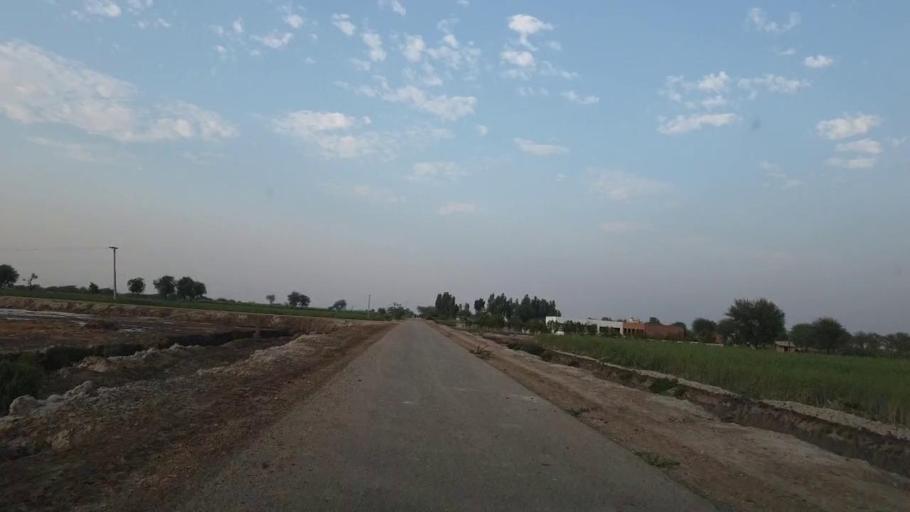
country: PK
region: Sindh
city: Pithoro
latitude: 25.5979
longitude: 69.3100
